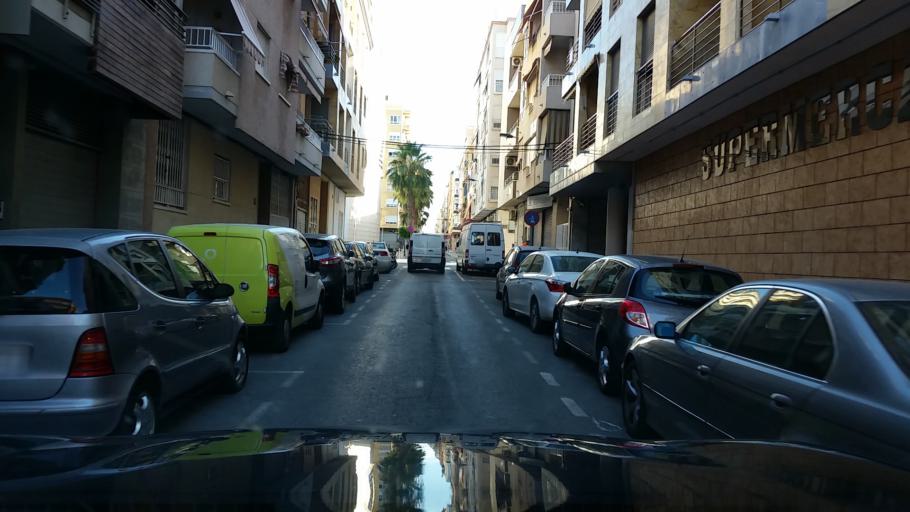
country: ES
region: Valencia
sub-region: Provincia de Alicante
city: Torrevieja
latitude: 37.9757
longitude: -0.6761
